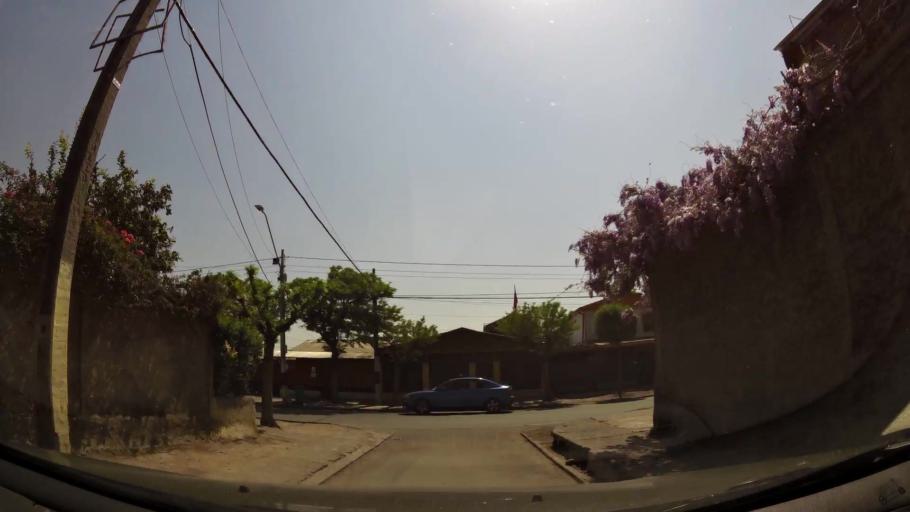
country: CL
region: Santiago Metropolitan
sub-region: Provincia de Maipo
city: San Bernardo
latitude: -33.5765
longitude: -70.7091
